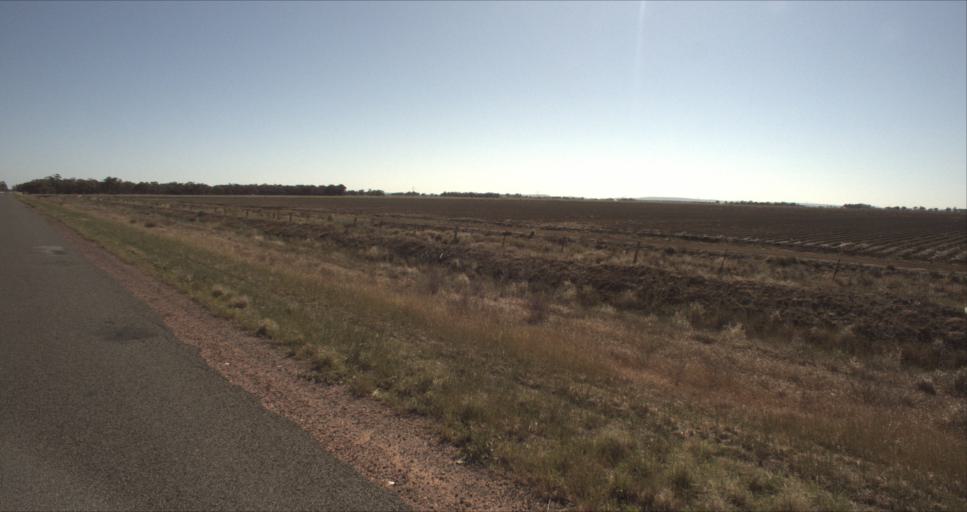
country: AU
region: New South Wales
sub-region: Leeton
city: Leeton
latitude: -34.5697
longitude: 146.2637
